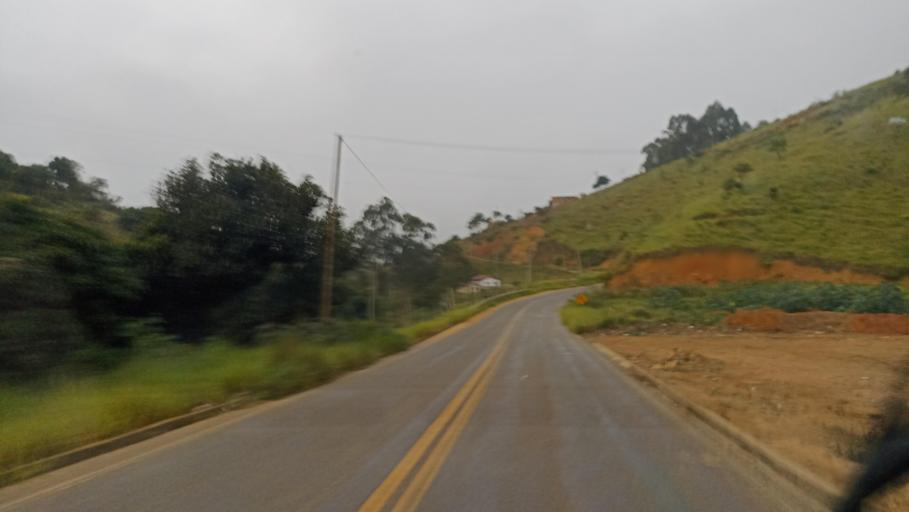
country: BR
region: Bahia
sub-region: Itanhem
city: Itanhem
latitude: -16.7351
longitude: -40.4321
